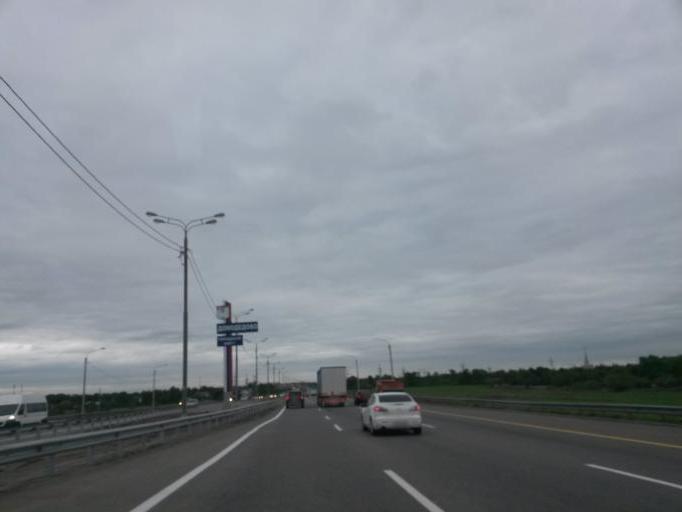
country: RU
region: Moskovskaya
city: Yam
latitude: 55.4952
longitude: 37.7322
